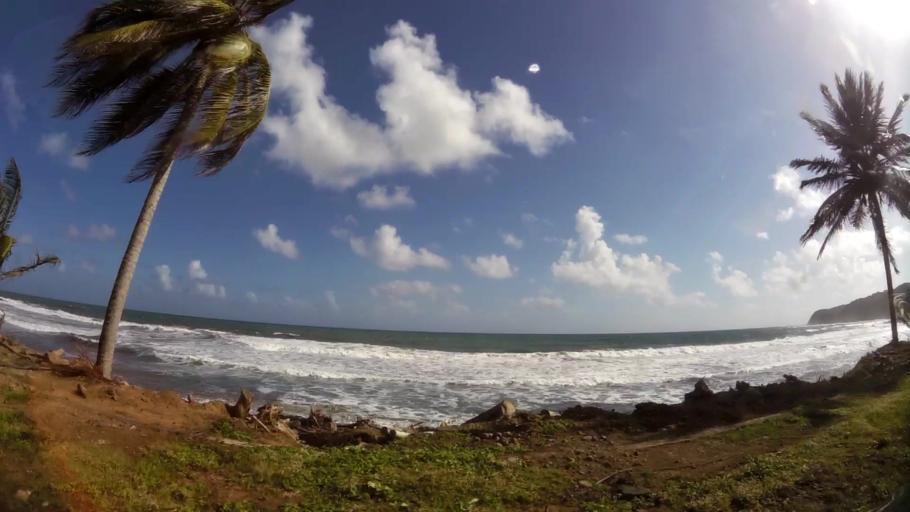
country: DM
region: Saint Andrew
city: Marigot
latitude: 15.5464
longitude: -61.2918
